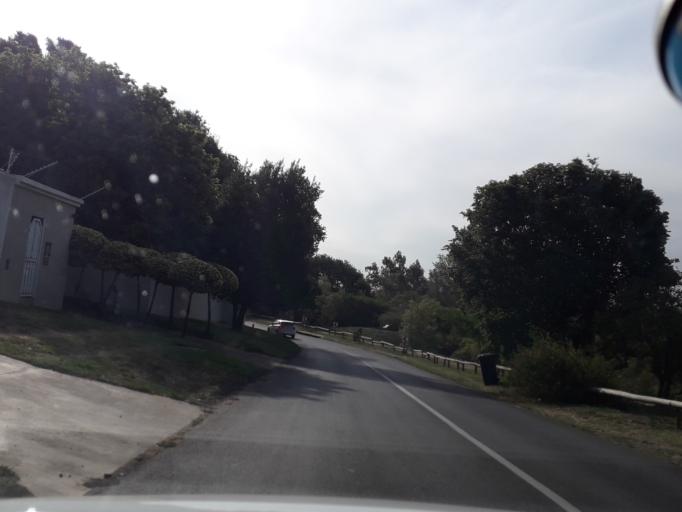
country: ZA
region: Gauteng
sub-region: City of Johannesburg Metropolitan Municipality
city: Diepsloot
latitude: -26.0478
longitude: 28.0090
